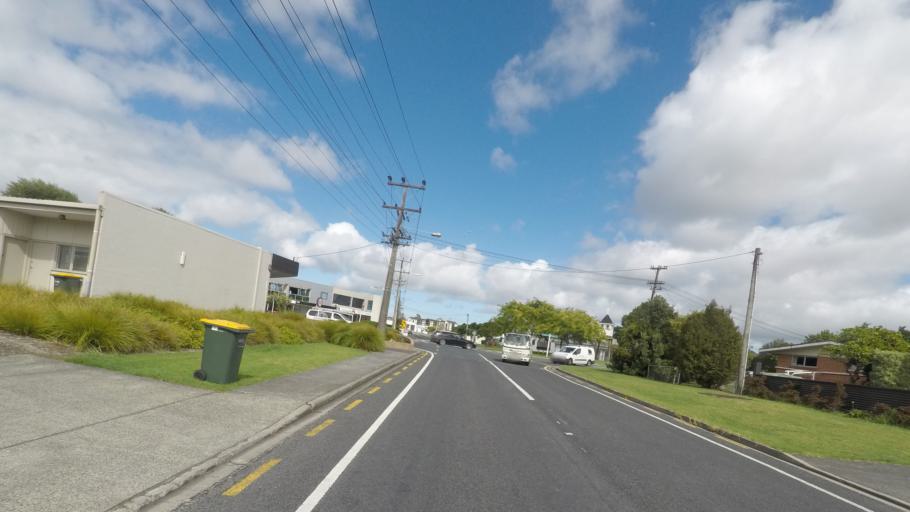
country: NZ
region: Auckland
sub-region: Auckland
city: Muriwai Beach
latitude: -36.7712
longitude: 174.5466
